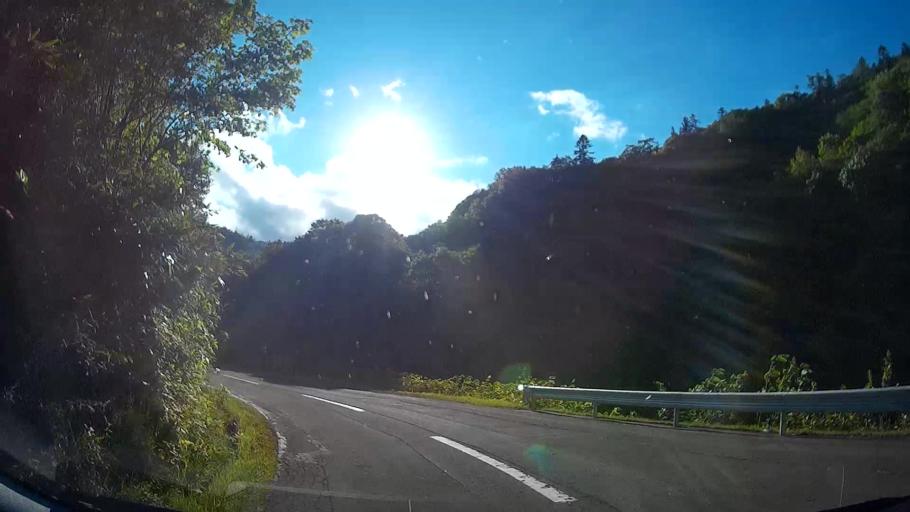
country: JP
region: Hokkaido
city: Otaru
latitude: 42.9825
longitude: 141.0423
